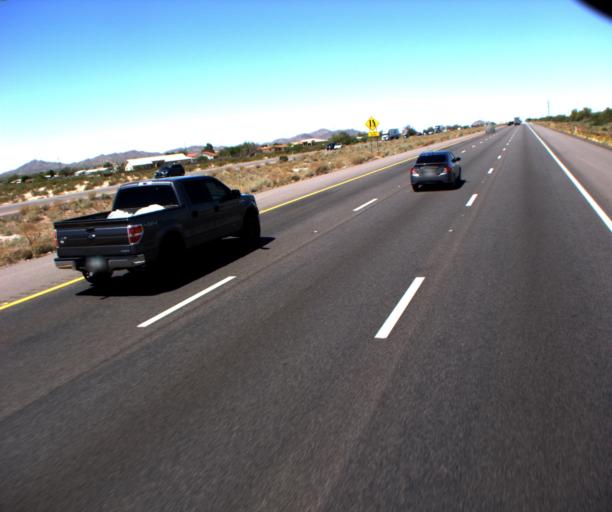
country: US
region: Arizona
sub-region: Pinal County
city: Casa Grande
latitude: 32.9760
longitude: -111.7309
